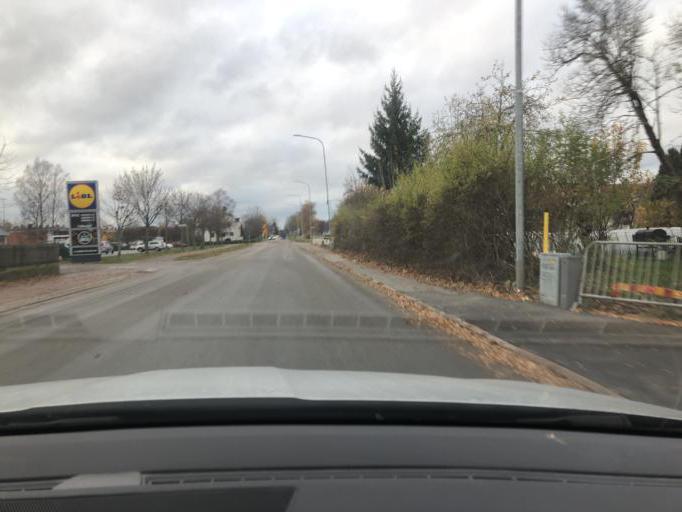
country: SE
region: Uppsala
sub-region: Tierps Kommun
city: Tierp
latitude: 60.3427
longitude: 17.5109
